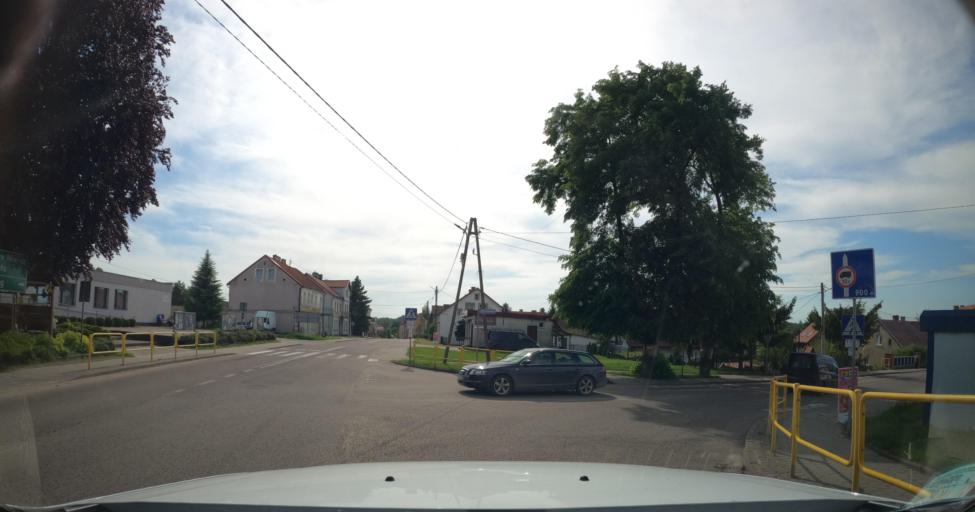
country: PL
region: Warmian-Masurian Voivodeship
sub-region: Powiat ostrodzki
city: Milakowo
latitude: 54.0084
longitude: 20.0697
